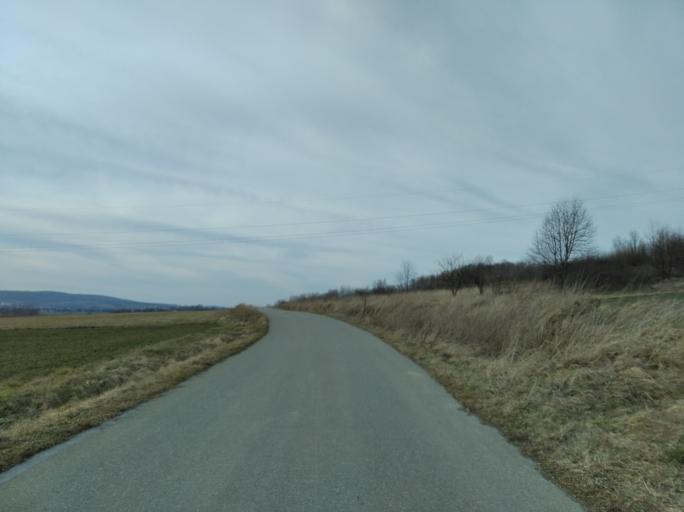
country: PL
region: Subcarpathian Voivodeship
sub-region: Powiat brzozowski
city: Gorki
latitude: 49.6562
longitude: 22.0261
